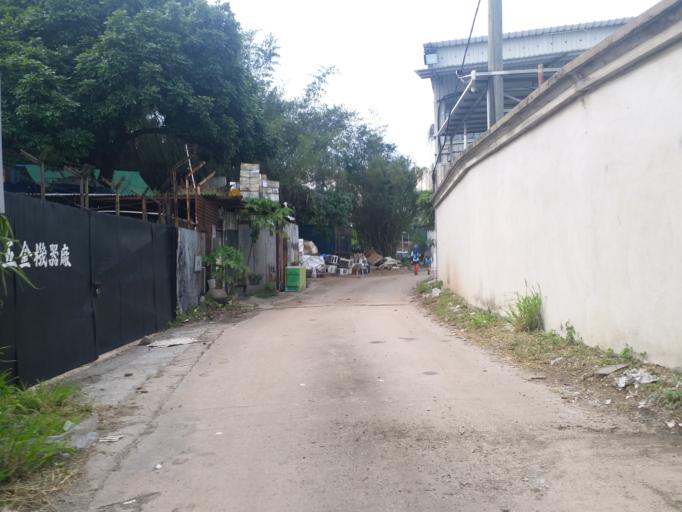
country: HK
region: Yuen Long
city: Yuen Long Kau Hui
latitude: 22.4399
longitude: 114.0017
